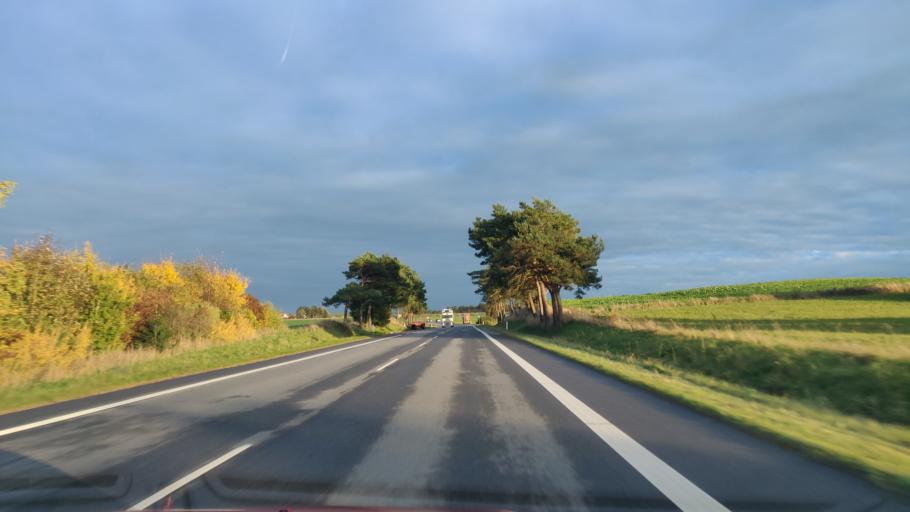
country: DK
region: Zealand
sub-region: Holbaek Kommune
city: Holbaek
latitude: 55.6843
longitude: 11.7137
